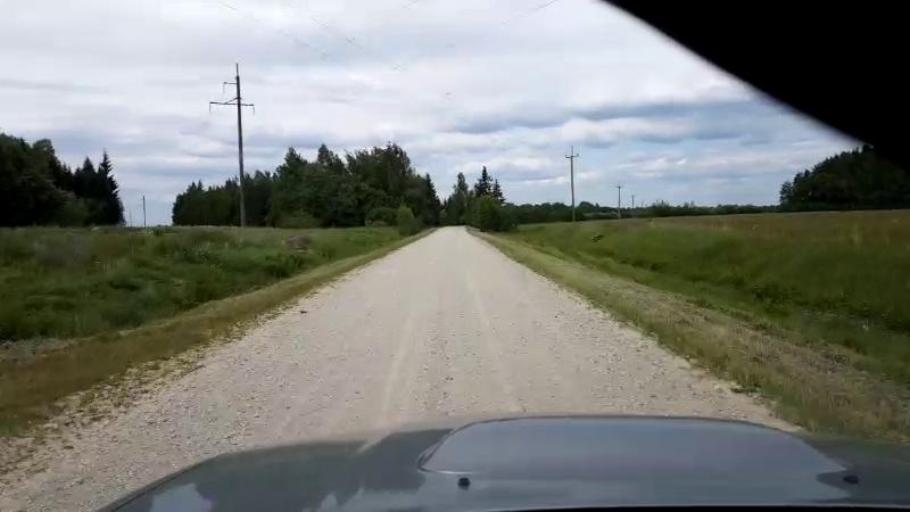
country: EE
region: Paernumaa
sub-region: Halinga vald
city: Parnu-Jaagupi
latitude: 58.5224
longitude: 24.5867
